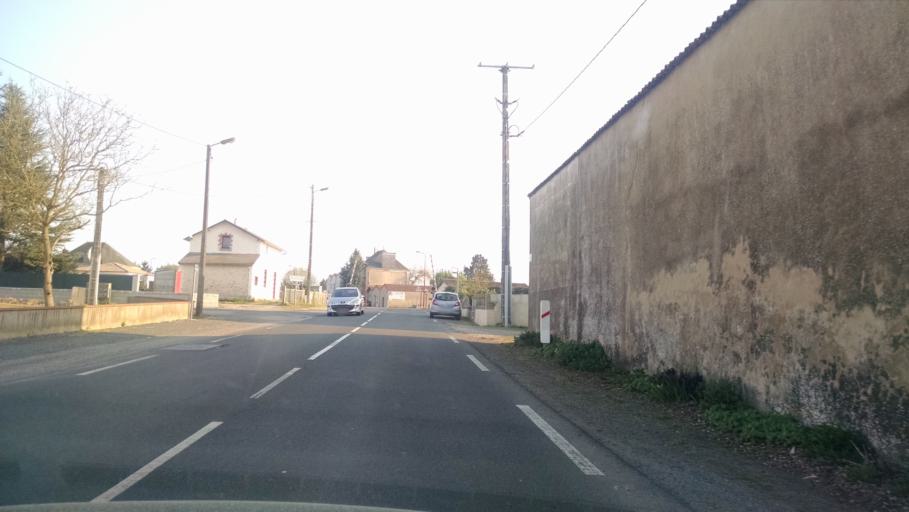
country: FR
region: Pays de la Loire
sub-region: Departement de la Loire-Atlantique
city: Boussay
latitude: 47.0515
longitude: -1.1846
